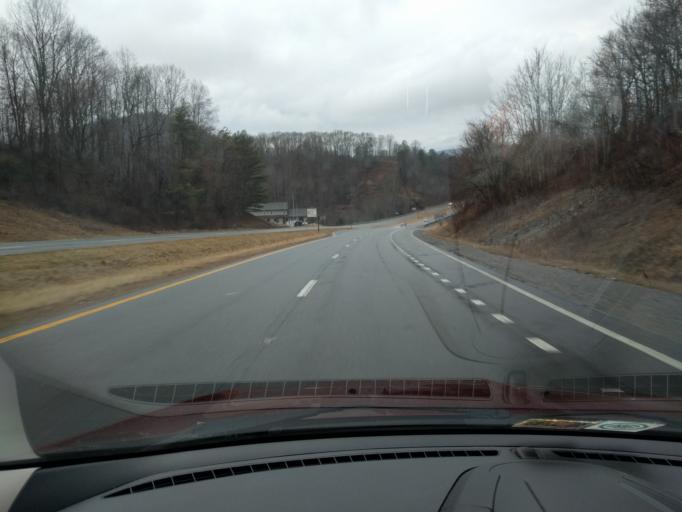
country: US
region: Virginia
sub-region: Montgomery County
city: Prices Fork
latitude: 37.2890
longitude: -80.4975
